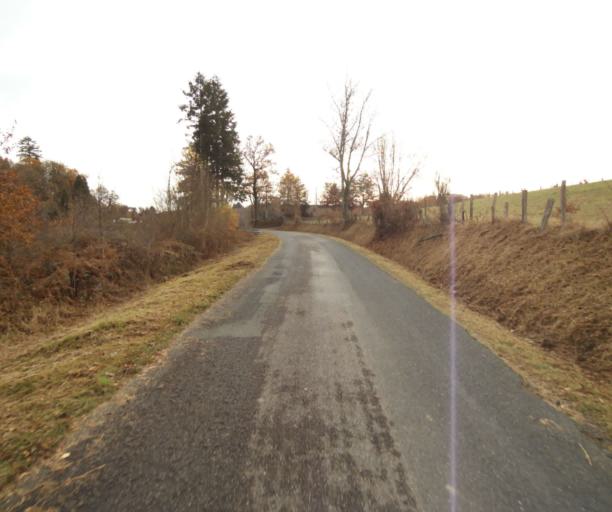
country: FR
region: Limousin
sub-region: Departement de la Correze
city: Sainte-Fortunade
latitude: 45.1782
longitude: 1.7821
